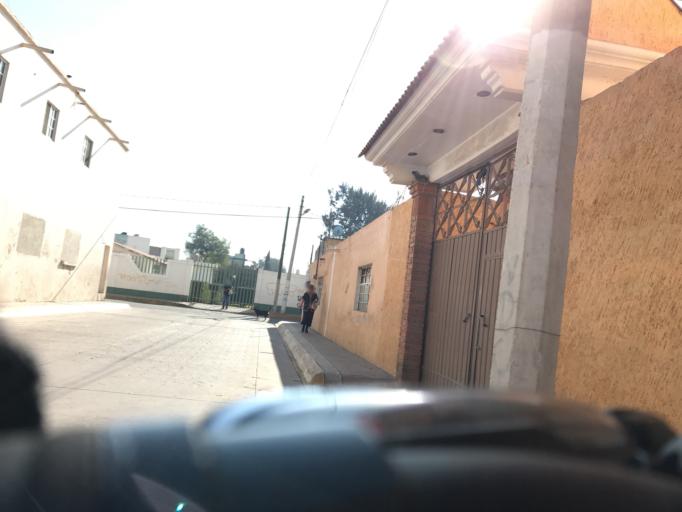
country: MX
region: Mexico
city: Santa Maria Tonatitla
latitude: 19.6876
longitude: -99.0536
